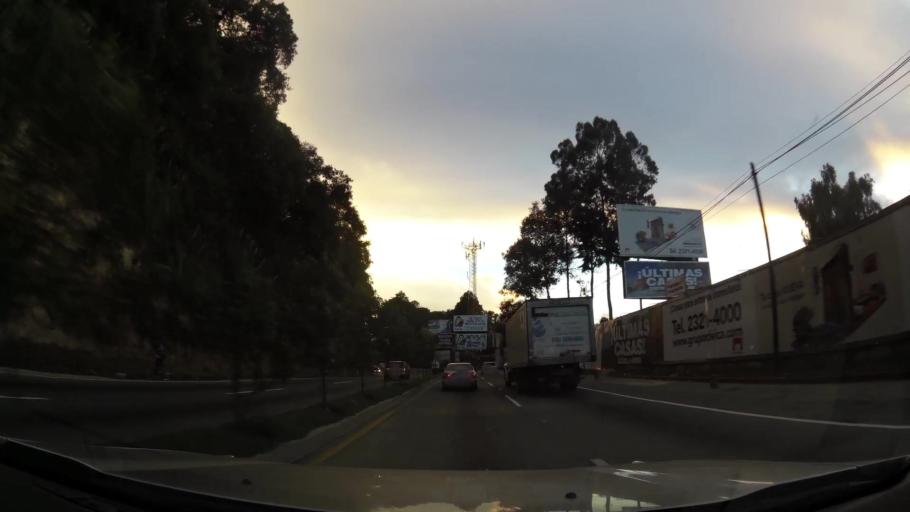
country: GT
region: Sacatepequez
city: San Lucas Sacatepequez
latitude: 14.6062
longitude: -90.6502
